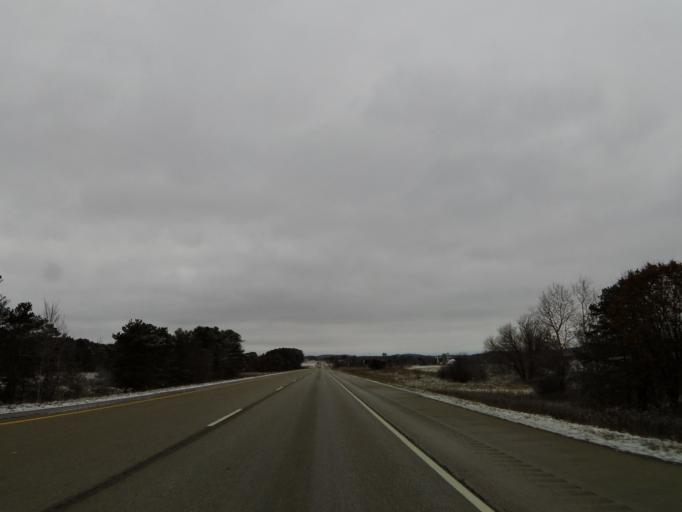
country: US
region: Wisconsin
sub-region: Trempealeau County
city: Osseo
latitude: 44.5267
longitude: -91.1488
